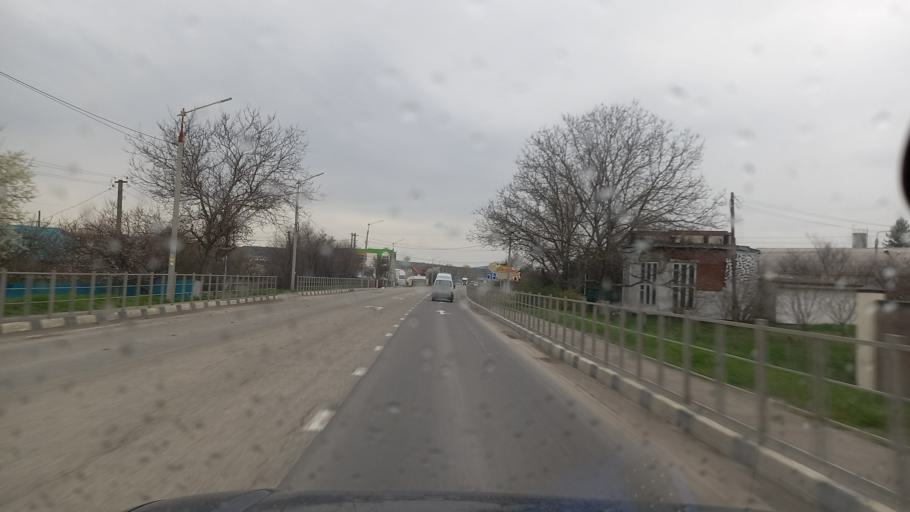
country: RU
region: Krasnodarskiy
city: Rayevskaya
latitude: 44.8968
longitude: 37.5636
